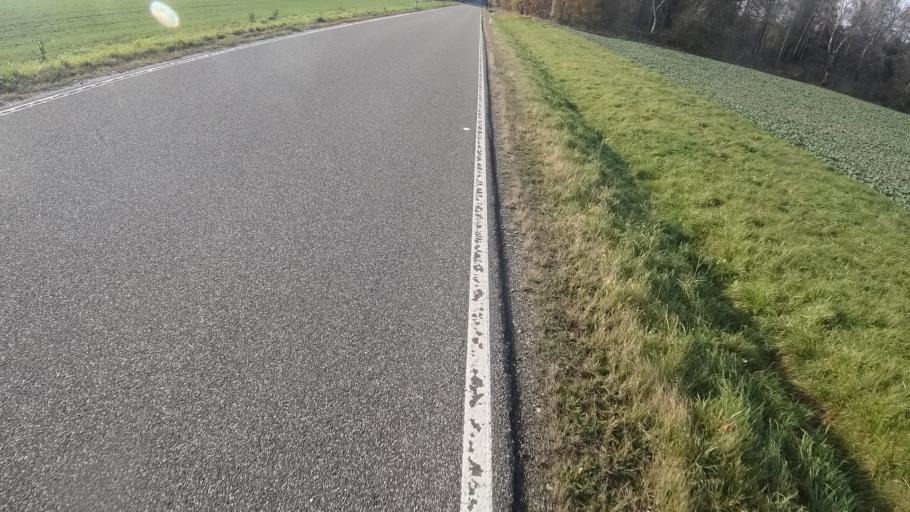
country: DE
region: Rheinland-Pfalz
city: Hausbay
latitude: 50.1084
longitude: 7.5473
